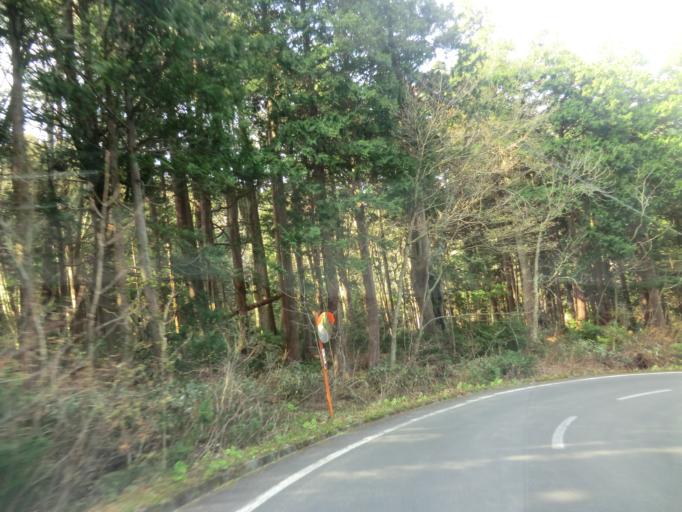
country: JP
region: Aomori
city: Mutsu
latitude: 41.3216
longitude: 141.1034
